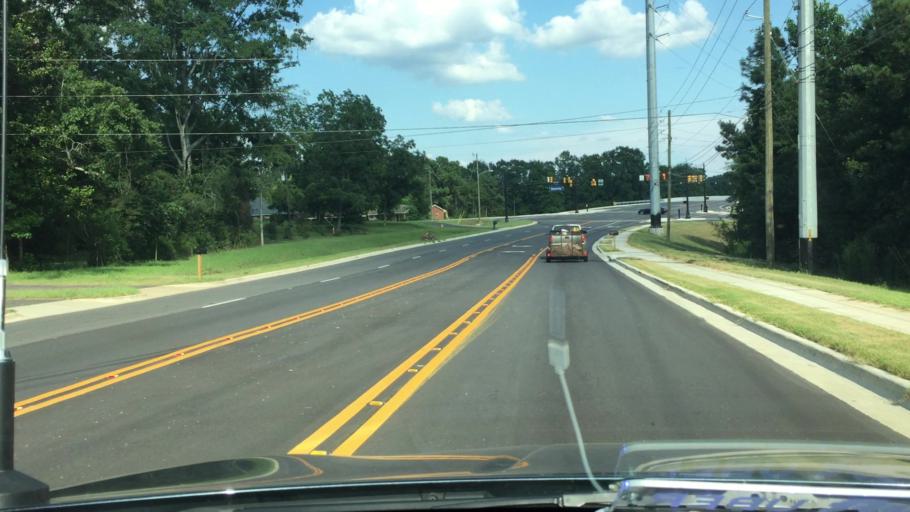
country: US
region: Alabama
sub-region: Lee County
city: Auburn
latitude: 32.5901
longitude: -85.4610
